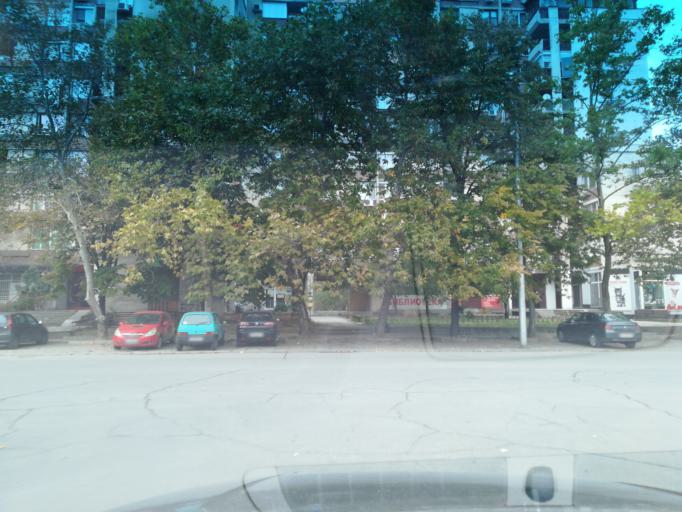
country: BG
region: Plovdiv
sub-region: Obshtina Plovdiv
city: Plovdiv
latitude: 42.1398
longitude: 24.7935
